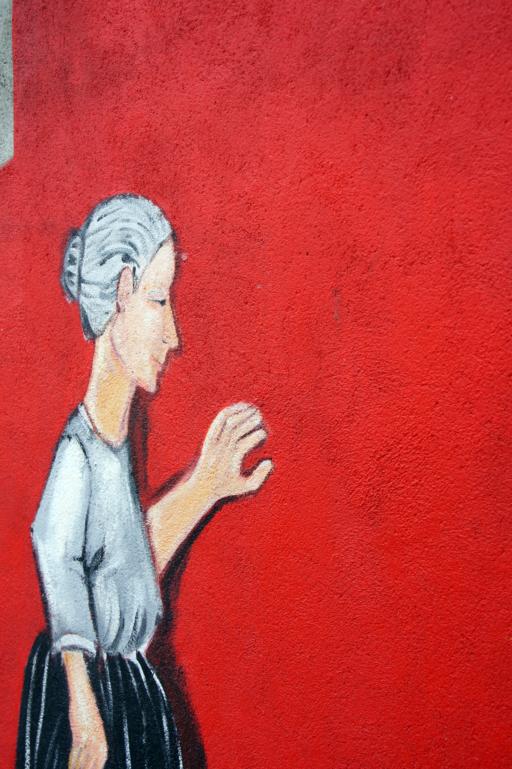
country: IT
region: Sardinia
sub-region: Provincia di Nuoro
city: Orgosolo
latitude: 40.2055
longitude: 9.3527
